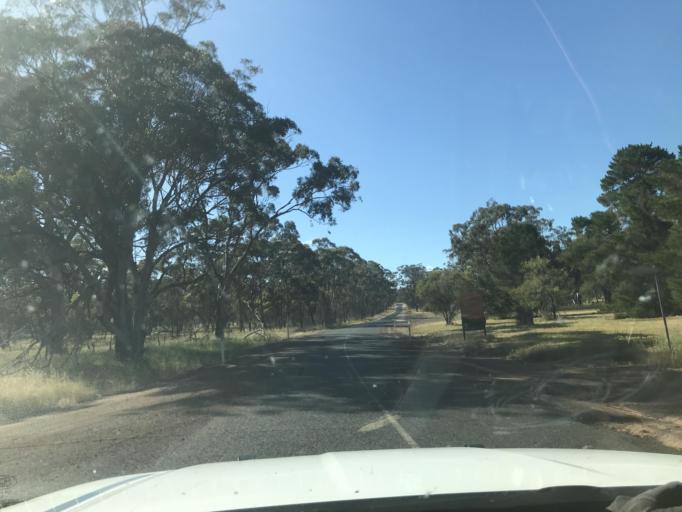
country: AU
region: Victoria
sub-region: Horsham
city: Horsham
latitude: -37.0933
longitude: 141.7736
